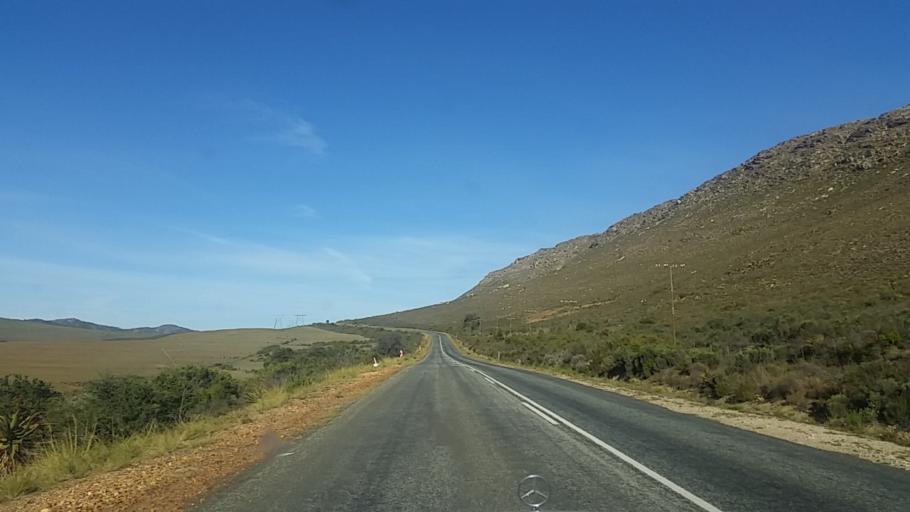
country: ZA
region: Western Cape
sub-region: Eden District Municipality
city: Knysna
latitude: -33.7427
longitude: 23.0167
